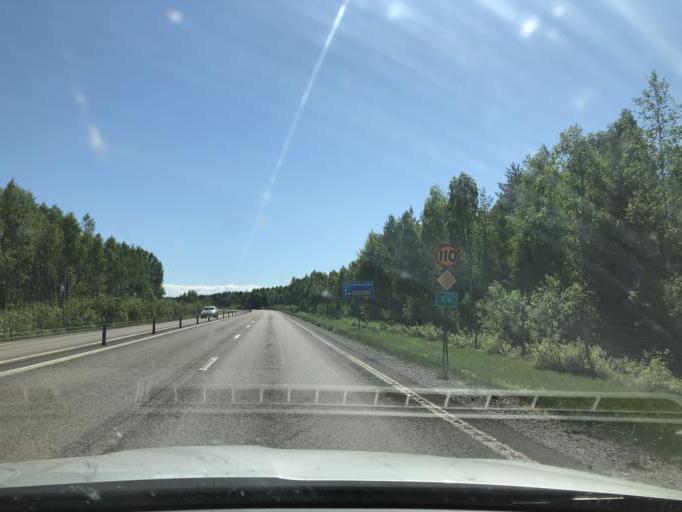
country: SE
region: Norrbotten
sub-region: Kalix Kommun
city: Rolfs
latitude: 65.8868
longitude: 22.9222
